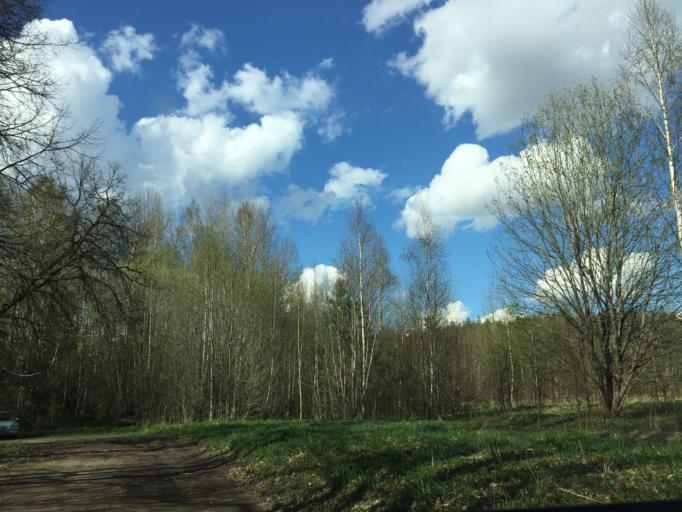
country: LV
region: Beverina
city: Murmuiza
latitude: 57.4123
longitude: 25.5268
